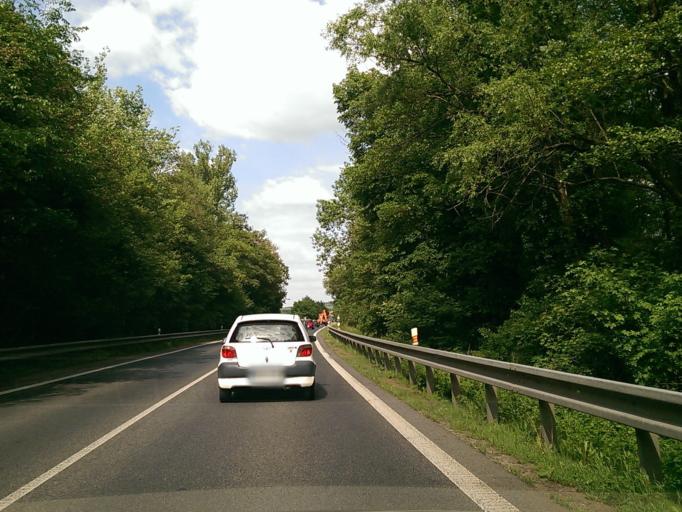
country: CZ
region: Central Bohemia
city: Libis
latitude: 50.2947
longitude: 14.5003
